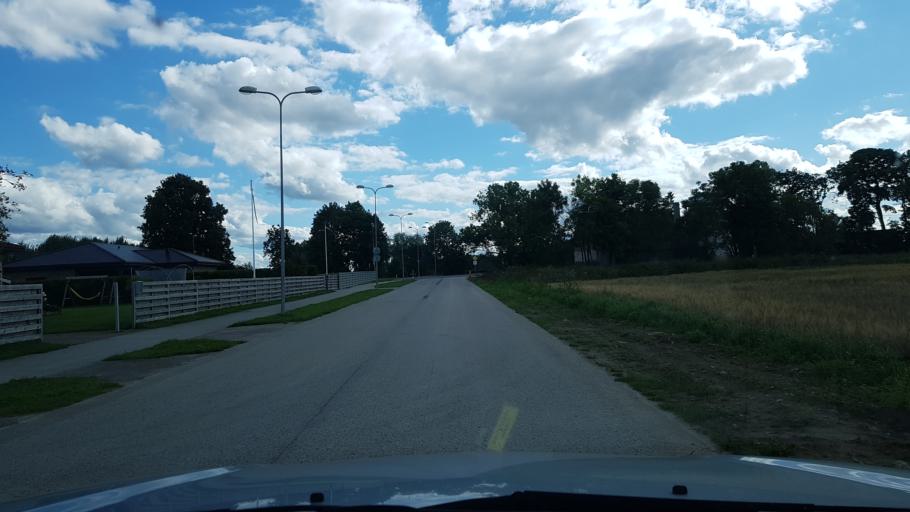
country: EE
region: Harju
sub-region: Rae vald
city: Jueri
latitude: 59.3739
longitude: 24.8324
